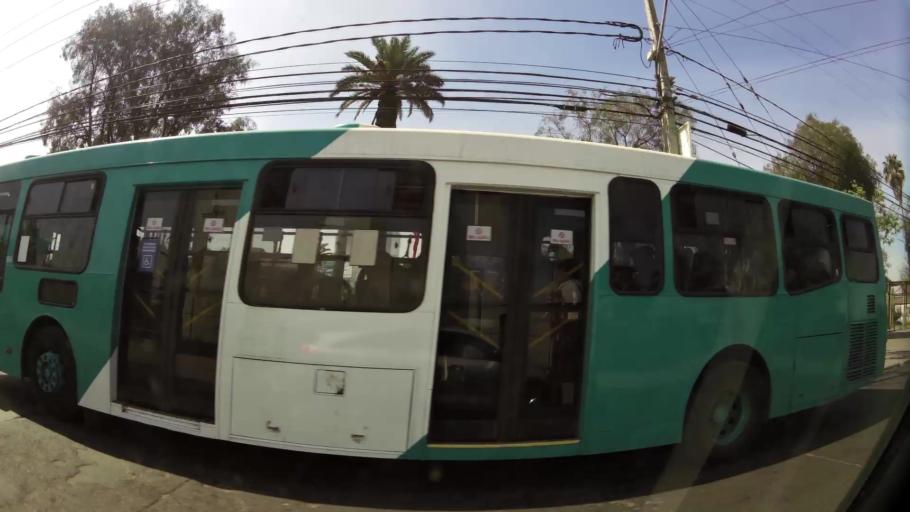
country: CL
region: Santiago Metropolitan
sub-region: Provincia de Santiago
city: Lo Prado
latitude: -33.4370
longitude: -70.7521
